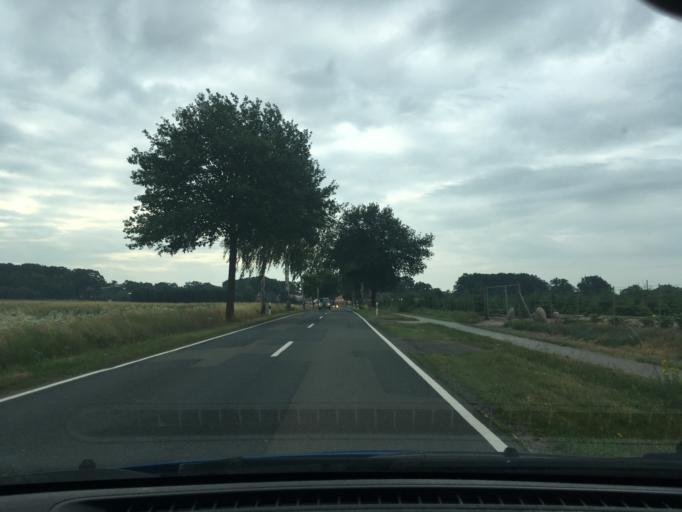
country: DE
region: Lower Saxony
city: Drestedt
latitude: 53.3315
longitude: 9.7637
